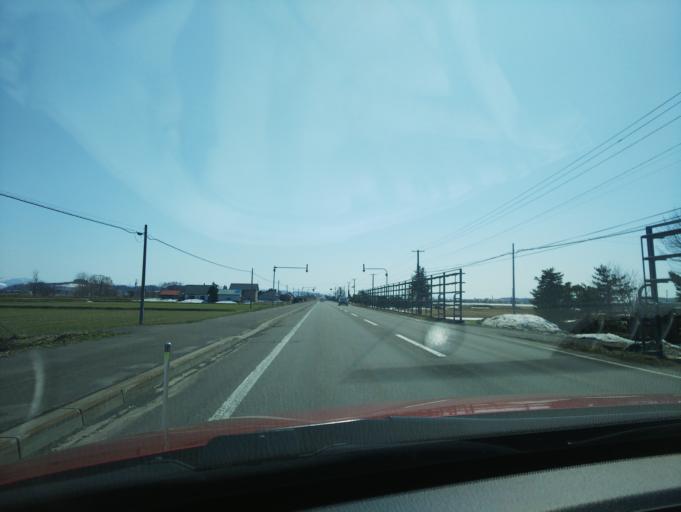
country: JP
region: Hokkaido
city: Nayoro
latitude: 44.2028
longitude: 142.3949
